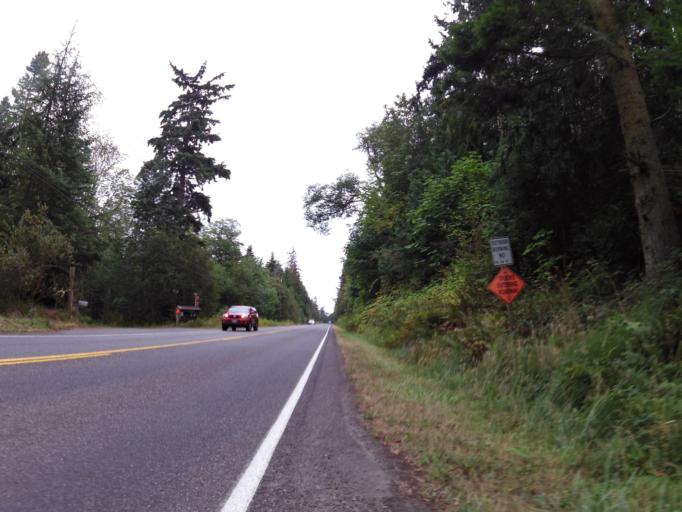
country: US
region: Washington
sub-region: Jefferson County
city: Port Ludlow
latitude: 47.9849
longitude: -122.7188
